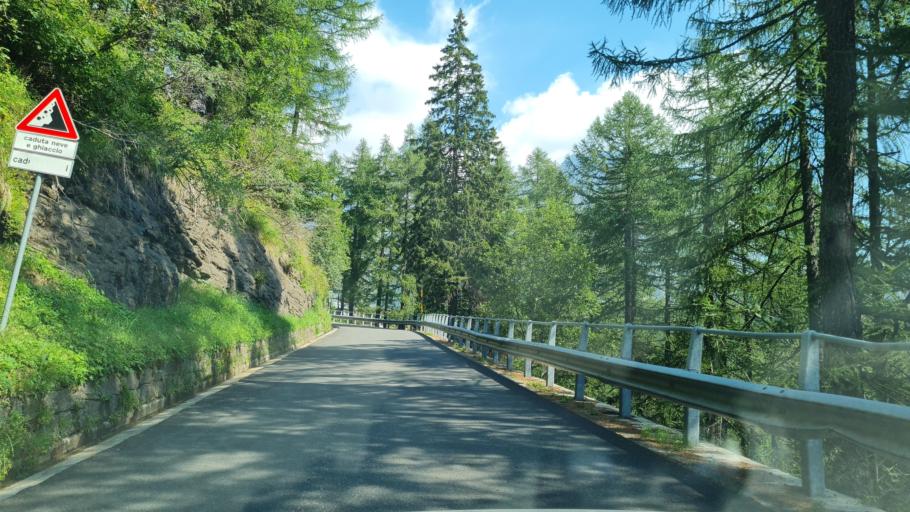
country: IT
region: Piedmont
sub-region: Provincia Verbano-Cusio-Ossola
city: Baceno
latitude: 46.3115
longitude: 8.2615
